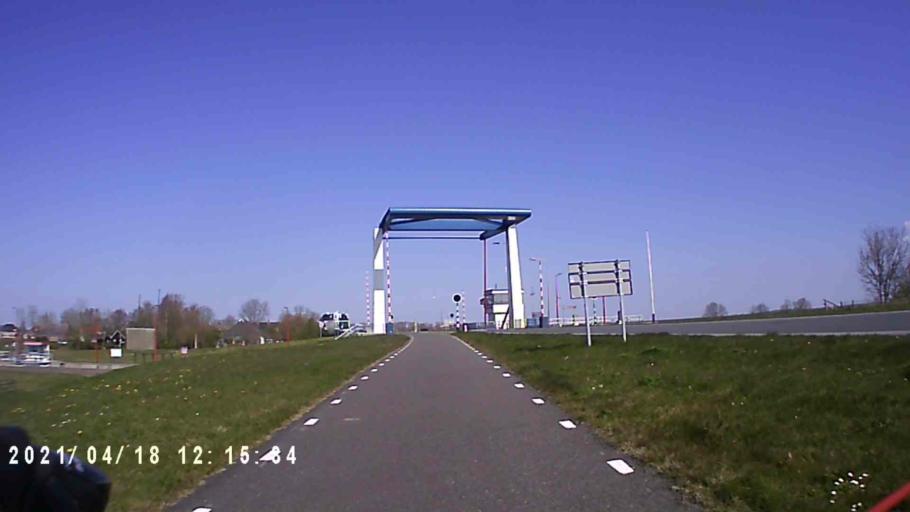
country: NL
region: Friesland
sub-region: Gemeente Kollumerland en Nieuwkruisland
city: Kollum
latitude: 53.3163
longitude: 6.1595
